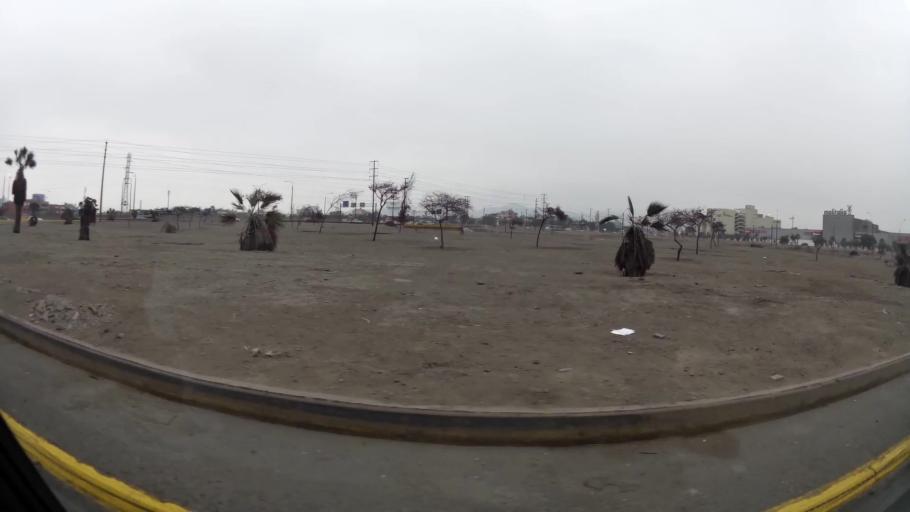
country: PE
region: Lima
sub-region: Lima
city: Independencia
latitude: -11.9634
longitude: -77.0672
